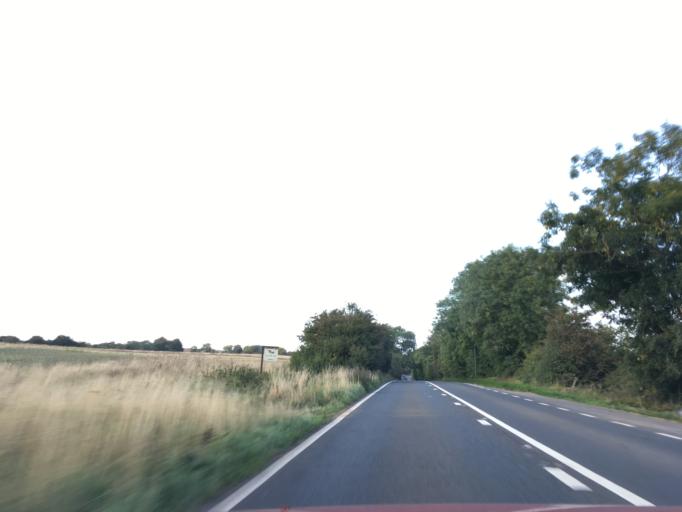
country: GB
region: England
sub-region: Gloucestershire
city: Northleach
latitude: 51.8617
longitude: -1.7994
